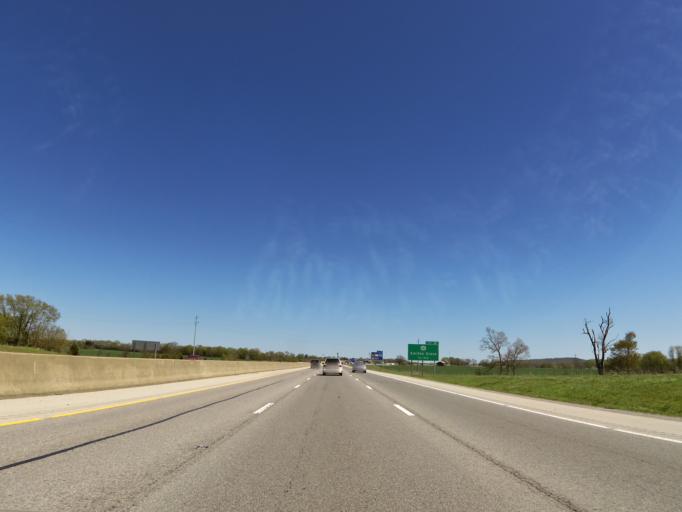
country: US
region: Kentucky
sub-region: Edmonson County
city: Brownsville
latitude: 37.0397
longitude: -86.2250
